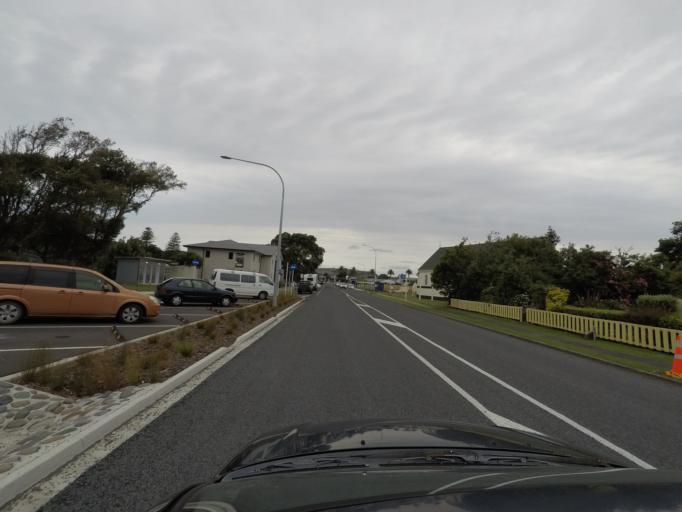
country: NZ
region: Waikato
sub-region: Waikato District
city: Raglan
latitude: -37.8026
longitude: 174.8686
